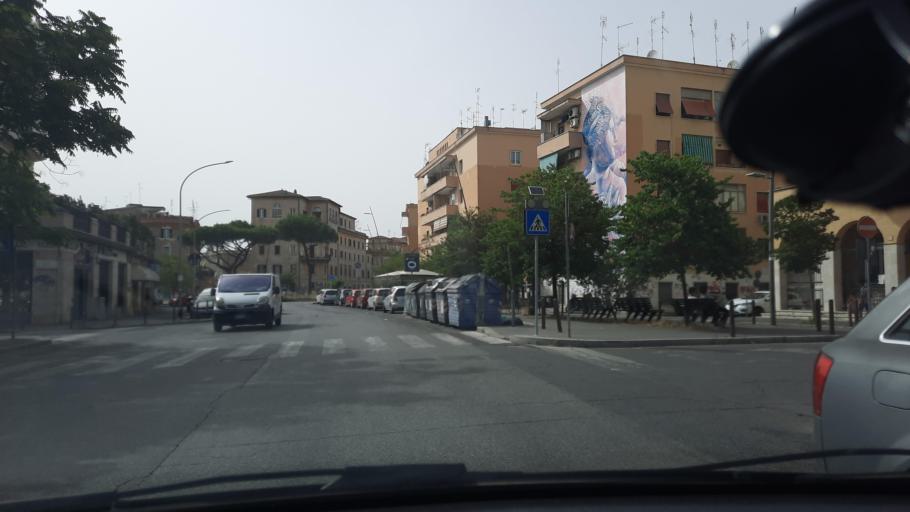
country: IT
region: Latium
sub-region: Citta metropolitana di Roma Capitale
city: Rome
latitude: 41.8605
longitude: 12.4870
